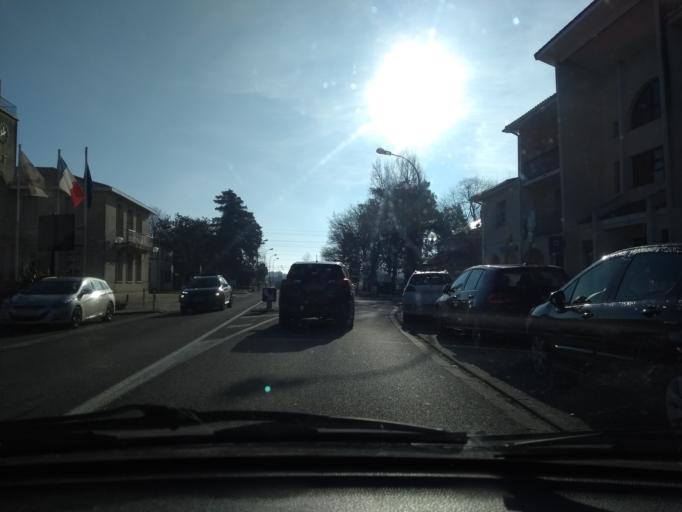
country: FR
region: Aquitaine
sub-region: Departement de la Gironde
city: Marcheprime
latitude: 44.6922
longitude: -0.8546
